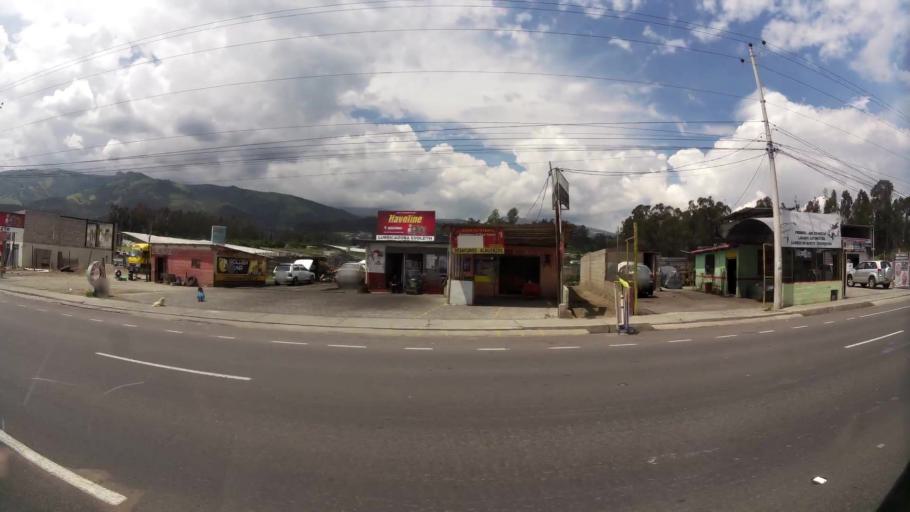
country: EC
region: Pichincha
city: Sangolqui
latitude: -0.2194
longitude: -78.3377
